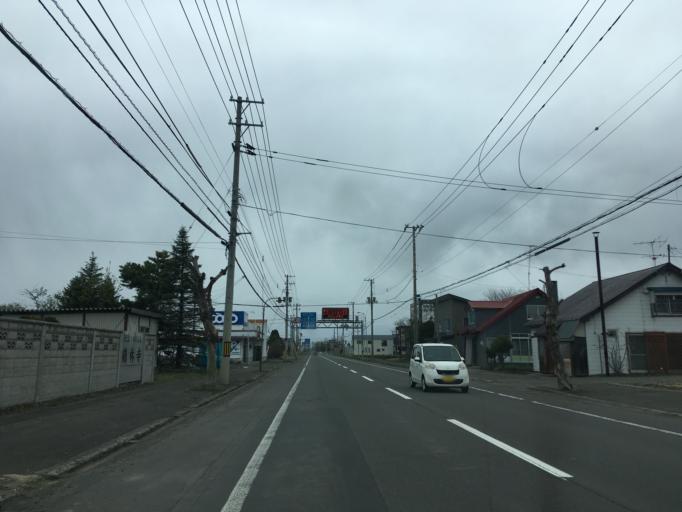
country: JP
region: Hokkaido
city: Chitose
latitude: 42.9464
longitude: 141.8034
